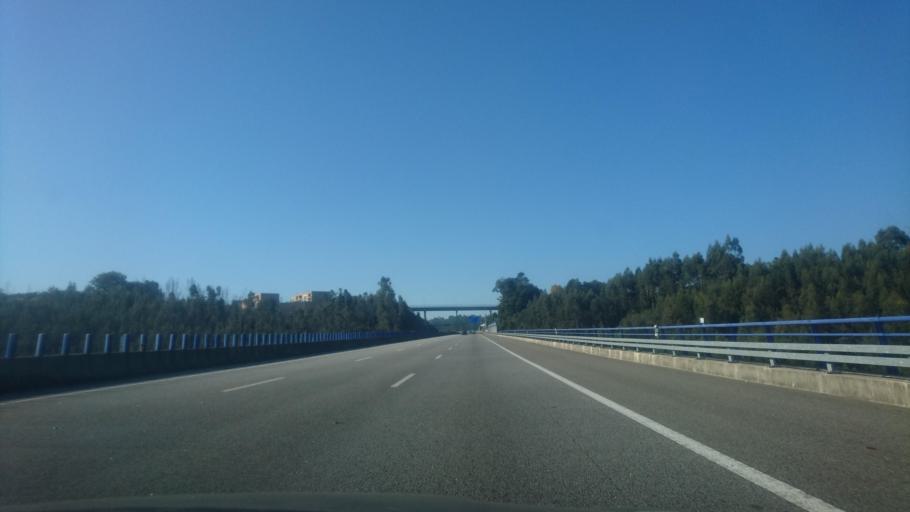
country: PT
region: Porto
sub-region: Vila Nova de Gaia
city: Sandim
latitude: 41.0619
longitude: -8.4610
